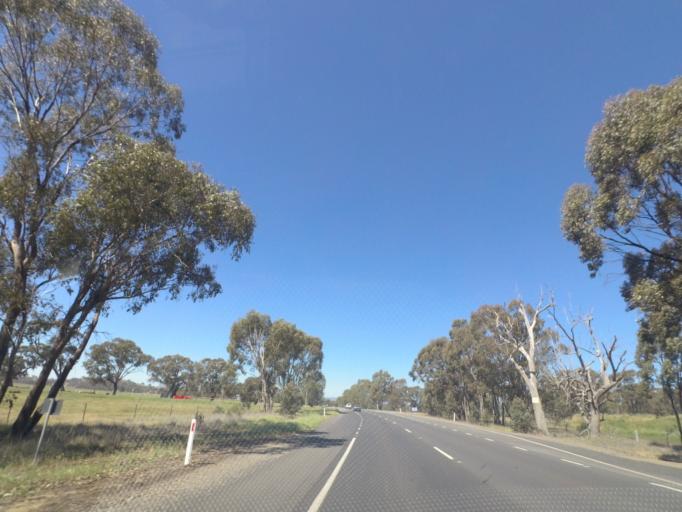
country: AU
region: Victoria
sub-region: Murrindindi
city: Kinglake West
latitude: -37.0298
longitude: 145.0840
